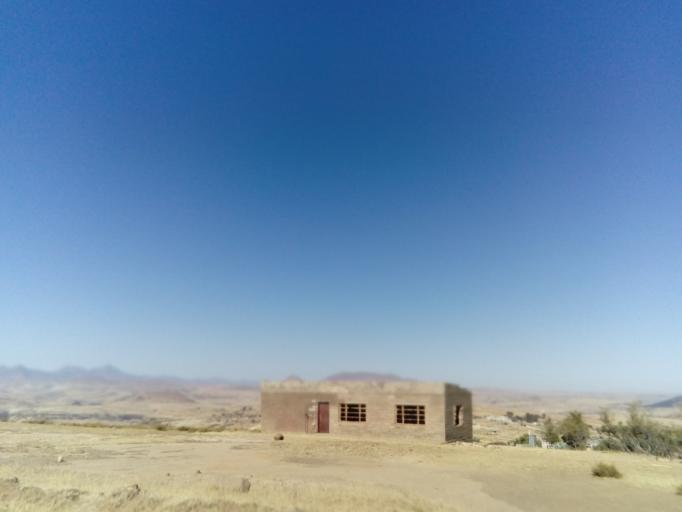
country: LS
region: Berea
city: Teyateyaneng
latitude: -29.1383
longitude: 27.8579
